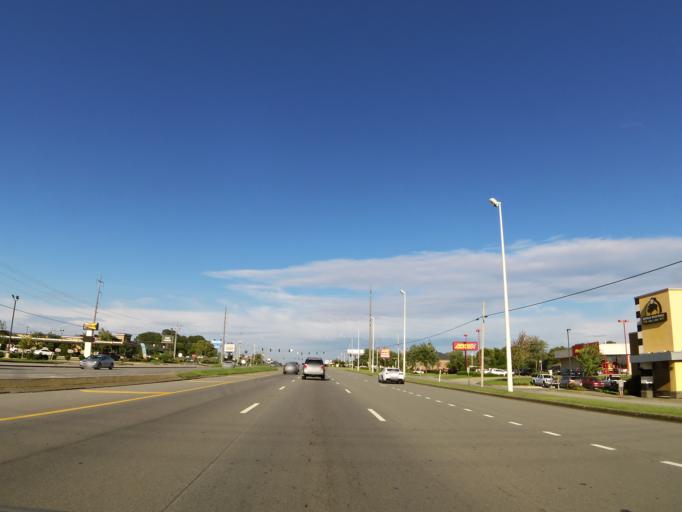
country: US
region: Alabama
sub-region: Lauderdale County
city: East Florence
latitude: 34.8304
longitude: -87.6256
